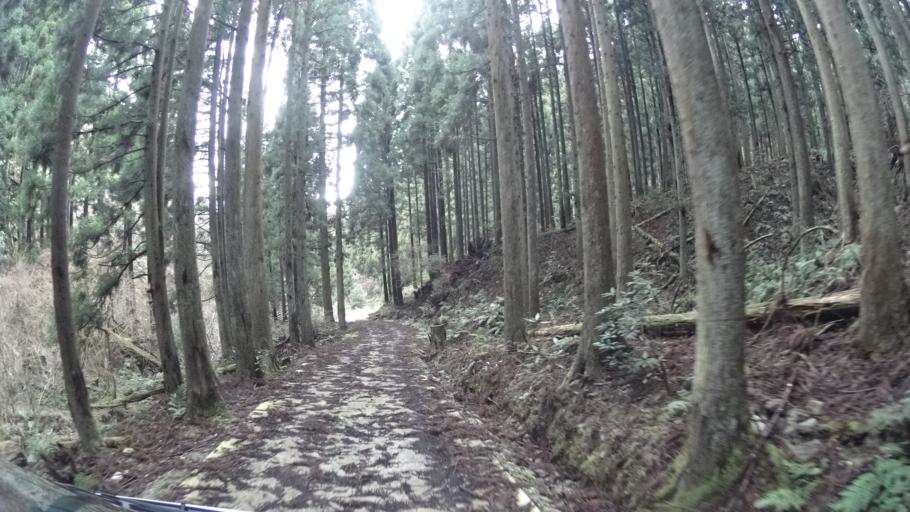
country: JP
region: Kyoto
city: Ayabe
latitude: 35.3089
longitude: 135.3773
